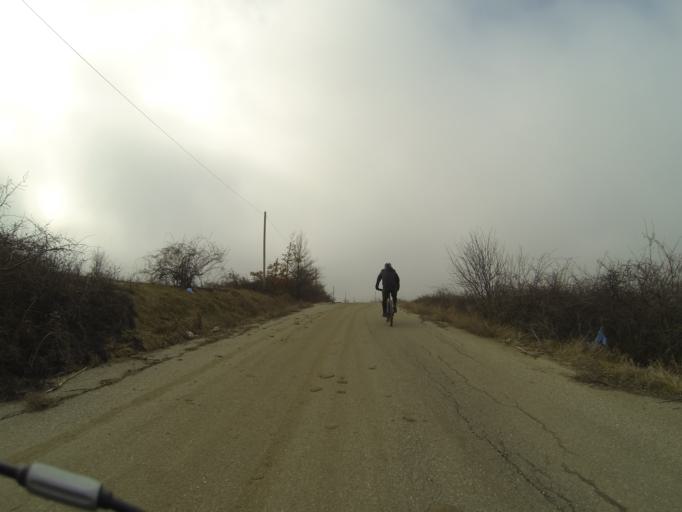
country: RO
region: Mehedinti
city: Dumbrava de Sus
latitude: 44.4921
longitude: 23.0864
